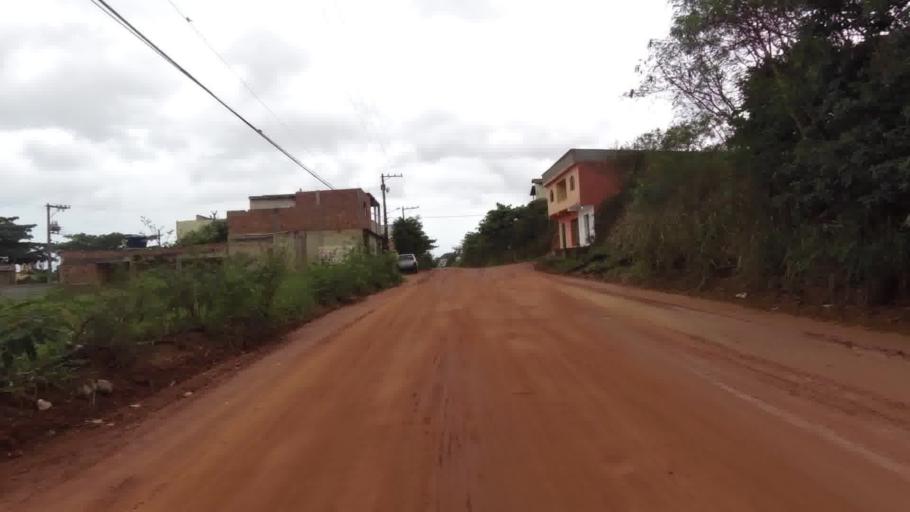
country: BR
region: Espirito Santo
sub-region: Marataizes
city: Marataizes
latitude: -21.0659
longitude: -40.8380
